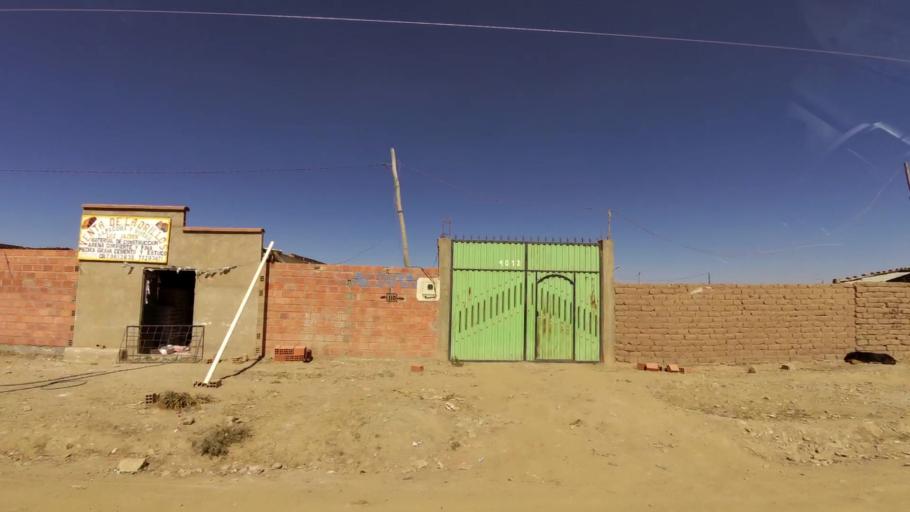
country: BO
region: La Paz
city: La Paz
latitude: -16.5856
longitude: -68.2068
